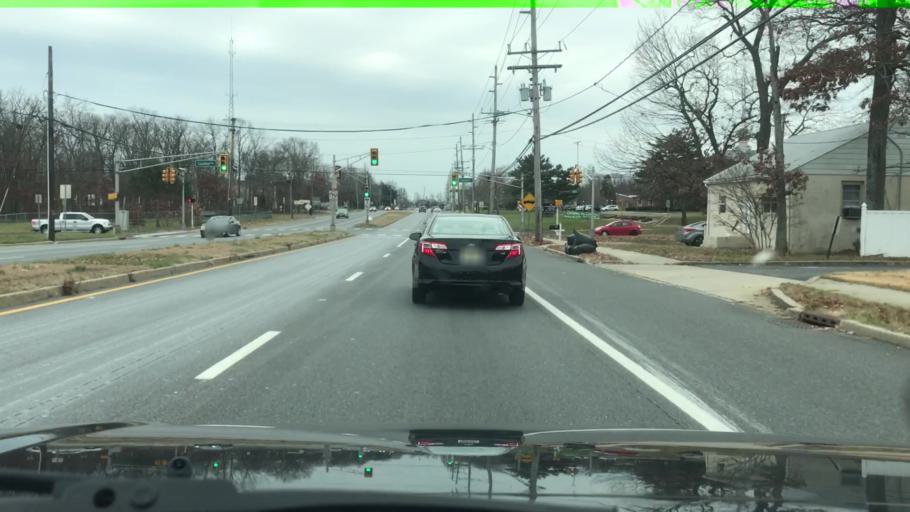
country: US
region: New Jersey
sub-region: Ocean County
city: Toms River
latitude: 39.9730
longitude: -74.1839
